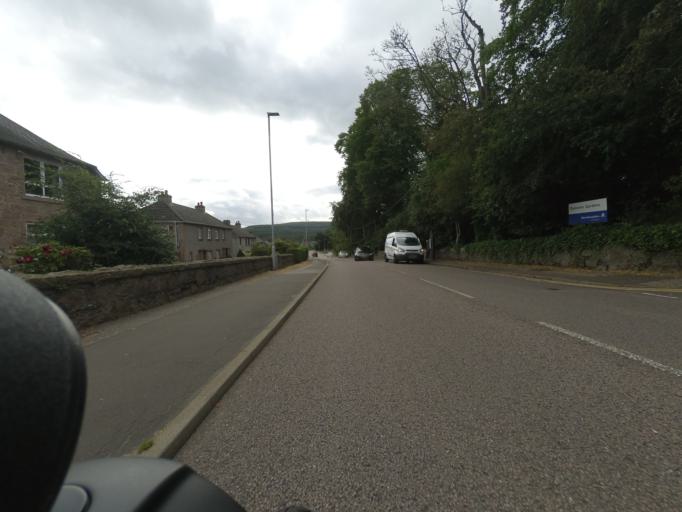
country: GB
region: Scotland
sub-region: Aberdeenshire
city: Banchory
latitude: 57.0550
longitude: -2.4909
